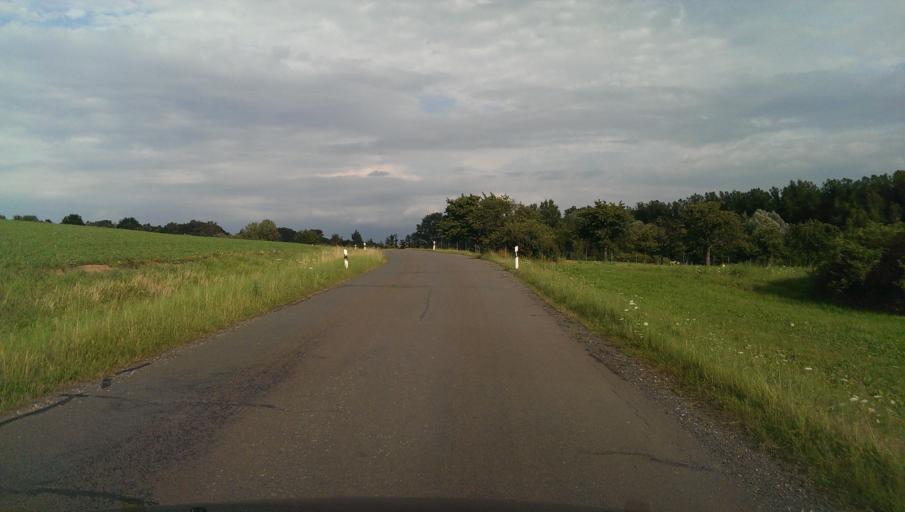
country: DE
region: Thuringia
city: Brahmenau
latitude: 50.9365
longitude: 12.1530
